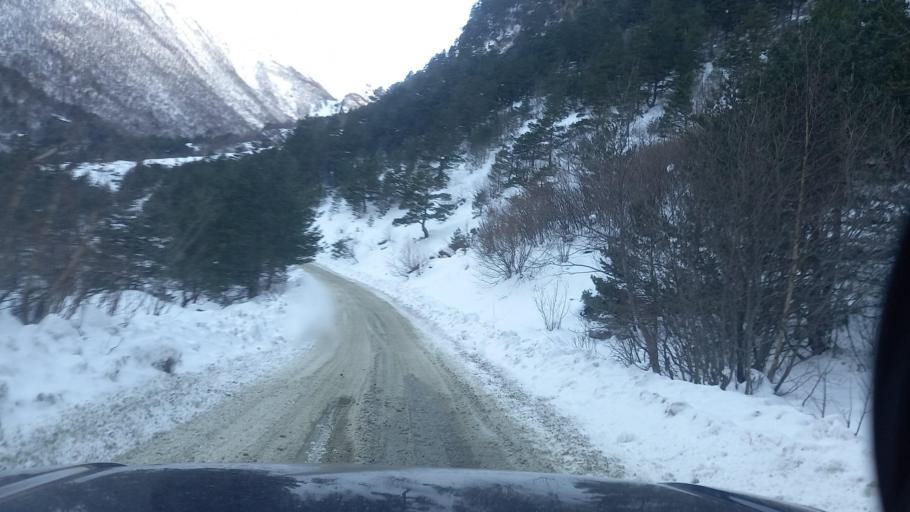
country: RU
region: Kabardino-Balkariya
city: Verkhnyaya Balkariya
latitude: 42.9023
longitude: 43.5901
